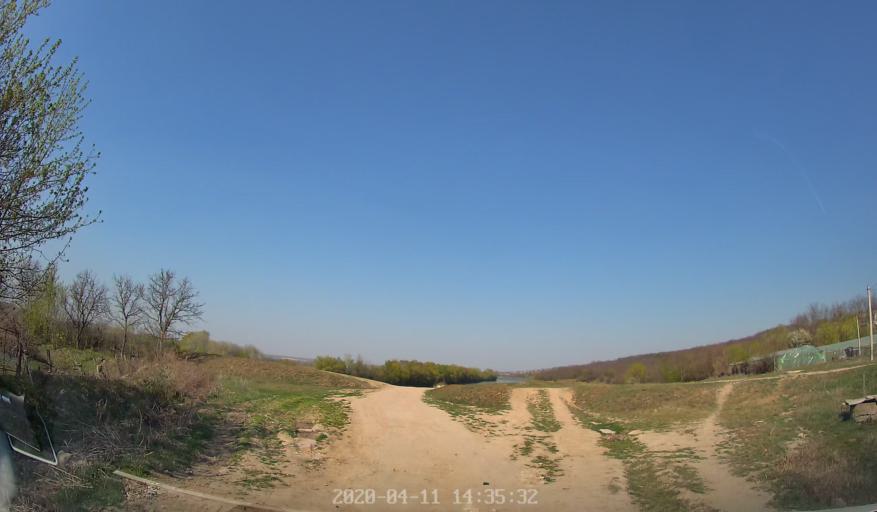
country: MD
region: Chisinau
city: Vadul lui Voda
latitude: 47.1025
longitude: 29.1764
